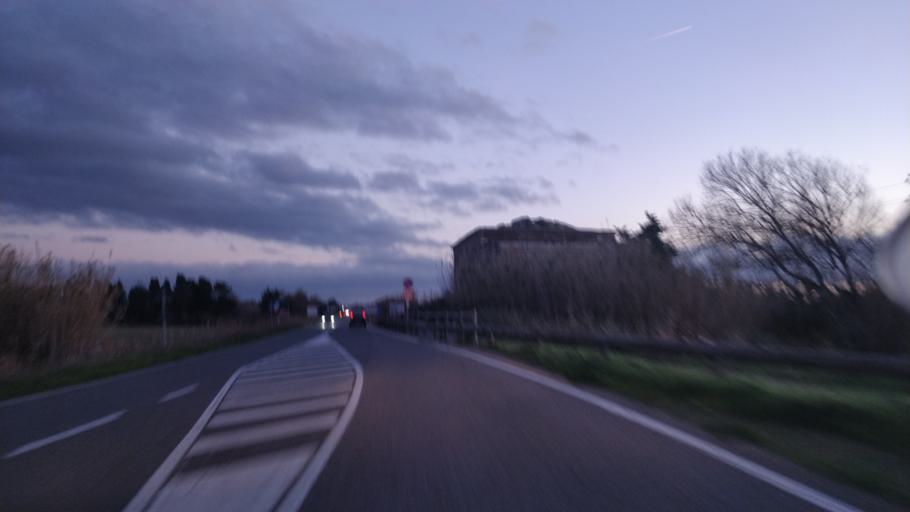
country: IT
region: Tuscany
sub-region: Provincia di Livorno
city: Vada
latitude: 43.3700
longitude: 10.4501
